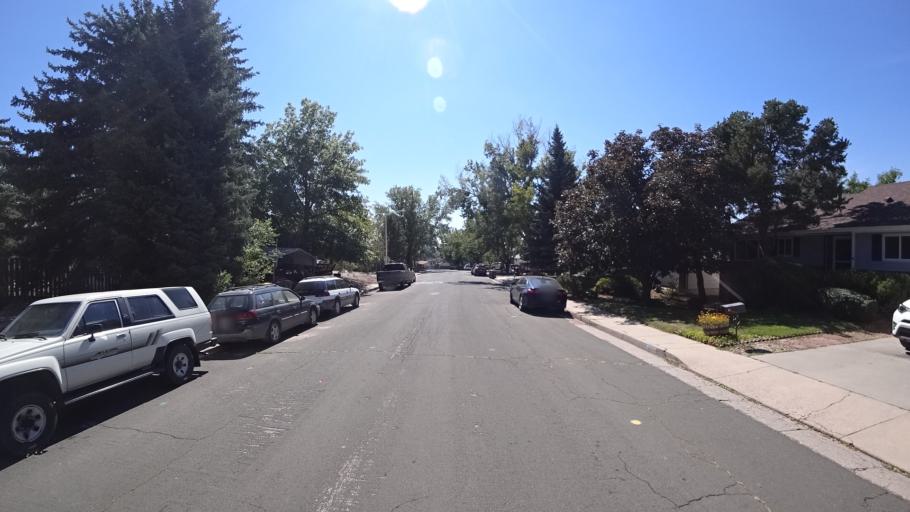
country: US
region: Colorado
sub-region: El Paso County
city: Cimarron Hills
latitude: 38.9079
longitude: -104.7681
